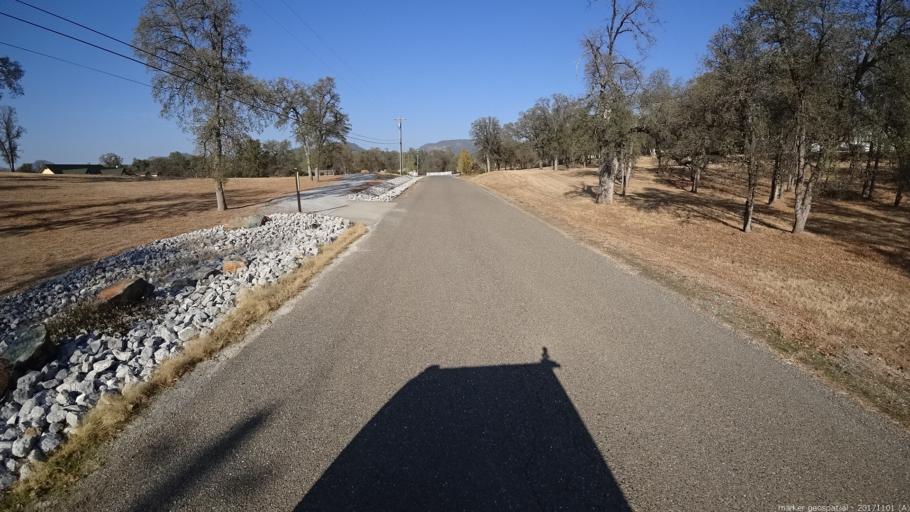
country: US
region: California
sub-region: Shasta County
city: Bella Vista
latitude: 40.6785
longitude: -122.2903
